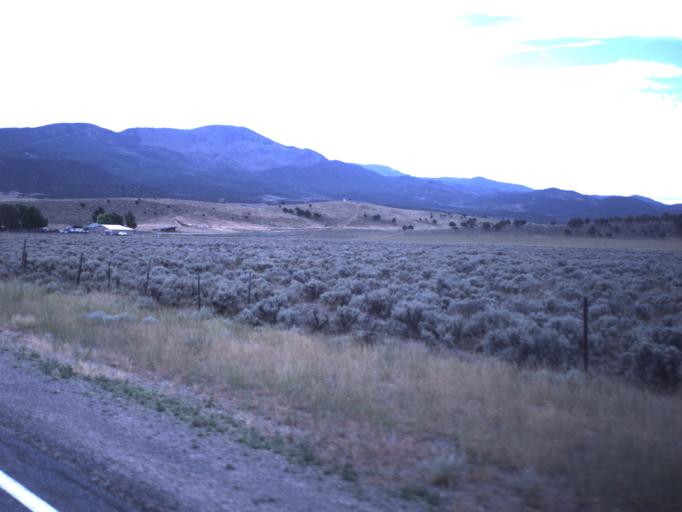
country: US
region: Utah
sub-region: Beaver County
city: Beaver
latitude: 38.6091
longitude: -112.5961
